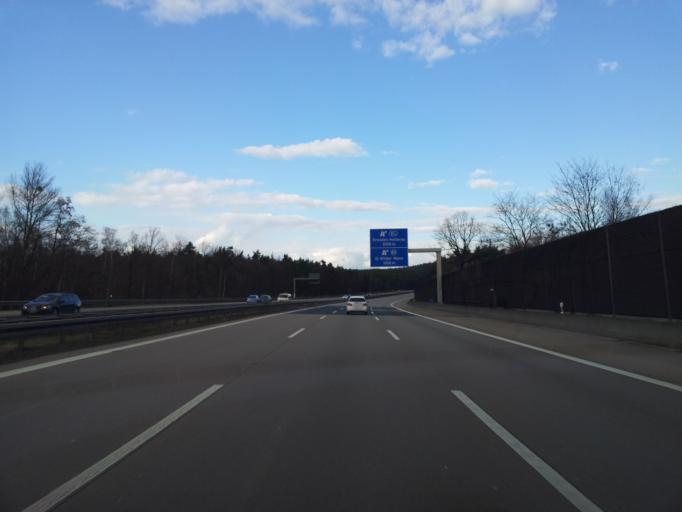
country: DE
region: Saxony
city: Radebeul
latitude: 51.0958
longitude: 13.6992
